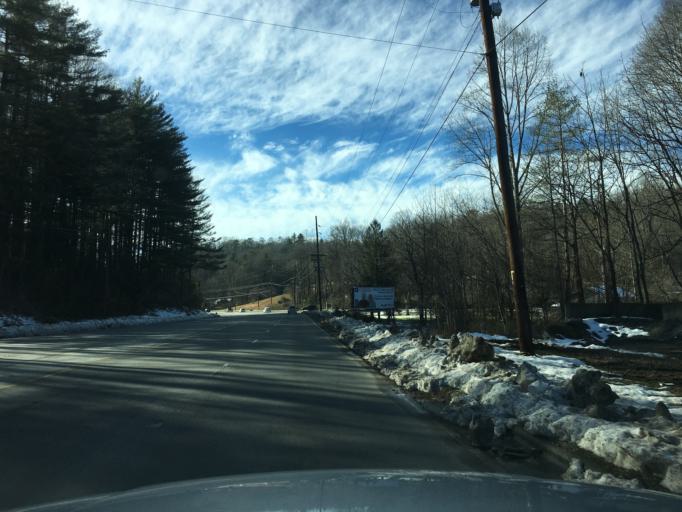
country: US
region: North Carolina
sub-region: Transylvania County
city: Brevard
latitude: 35.2214
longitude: -82.7455
